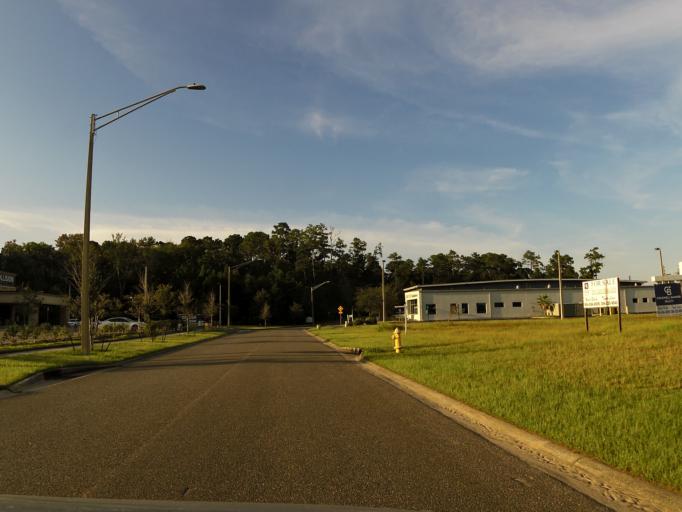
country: US
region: Florida
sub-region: Clay County
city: Orange Park
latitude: 30.2251
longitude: -81.7027
